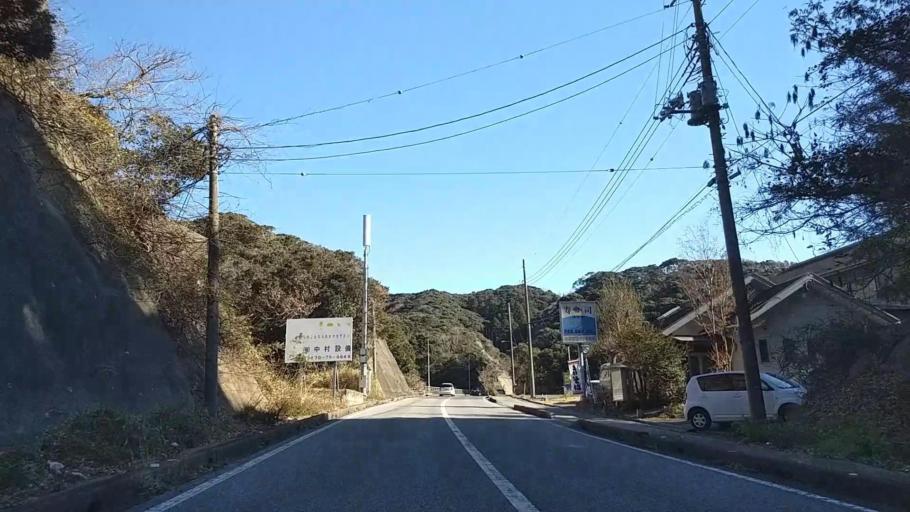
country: JP
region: Chiba
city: Katsuura
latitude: 35.1431
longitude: 140.2644
